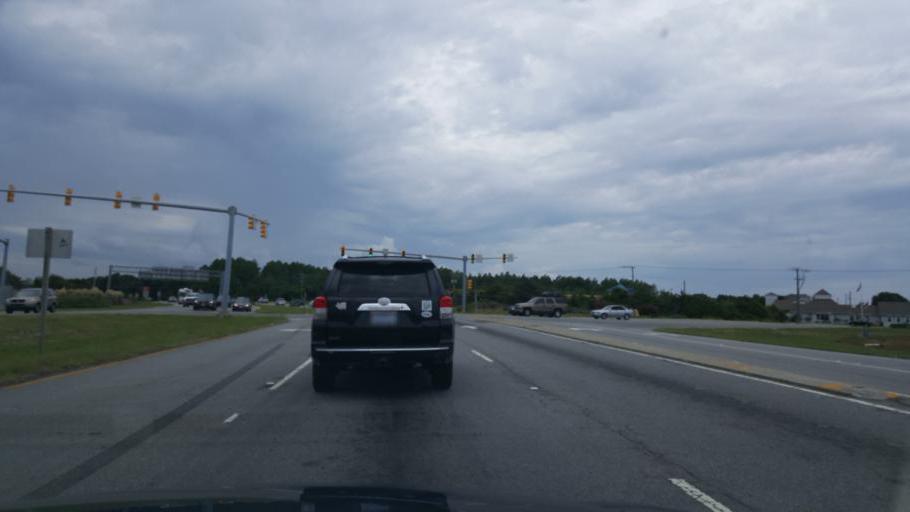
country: US
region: North Carolina
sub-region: Dare County
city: Kitty Hawk
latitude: 36.0990
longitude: -75.7141
